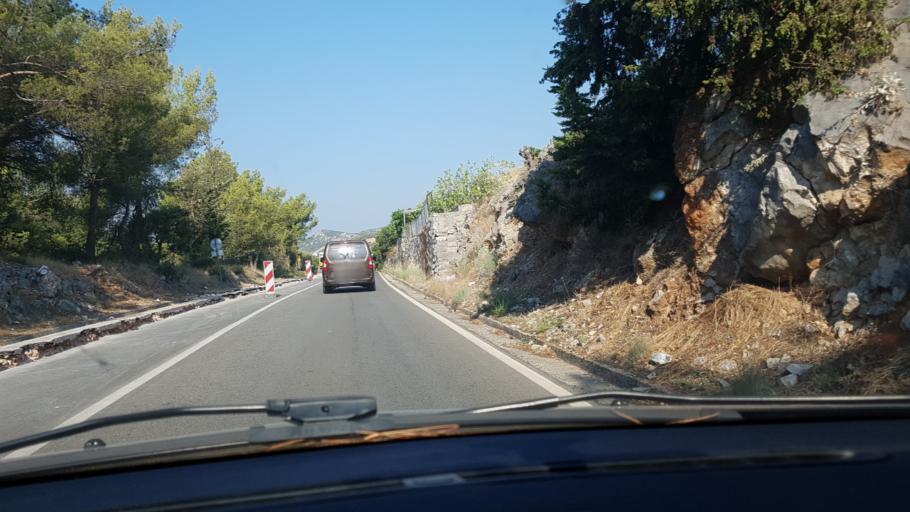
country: HR
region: Splitsko-Dalmatinska
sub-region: Grad Trogir
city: Trogir
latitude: 43.5144
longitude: 16.2033
